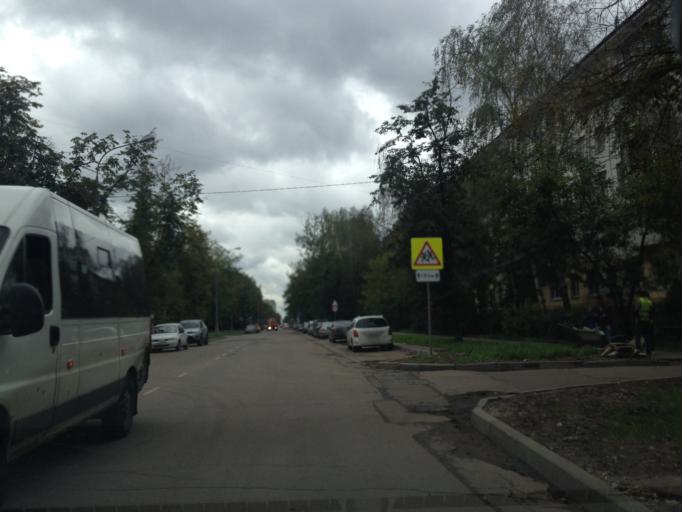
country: RU
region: Moscow
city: Gol'yanovo
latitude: 55.8093
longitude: 37.8048
